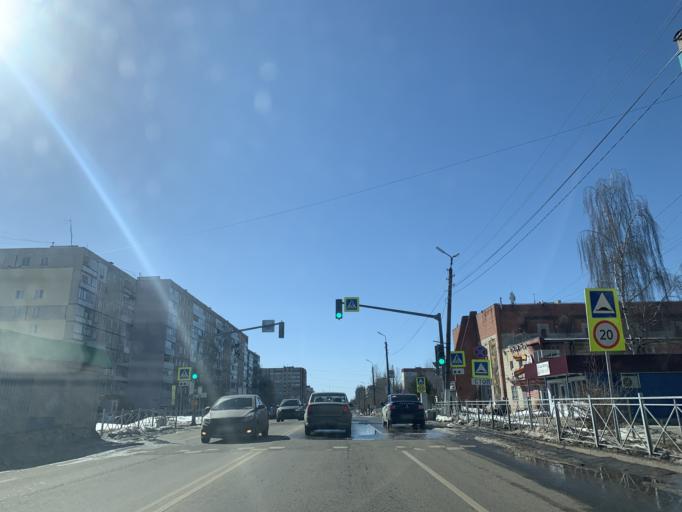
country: RU
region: Jaroslavl
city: Tutayev
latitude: 57.8681
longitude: 39.5114
